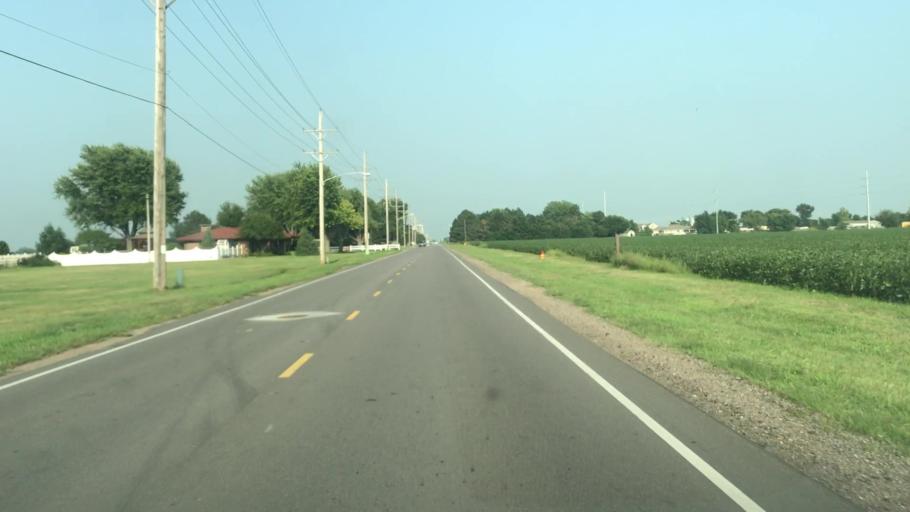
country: US
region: Nebraska
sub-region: Hall County
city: Grand Island
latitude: 40.9456
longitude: -98.3303
